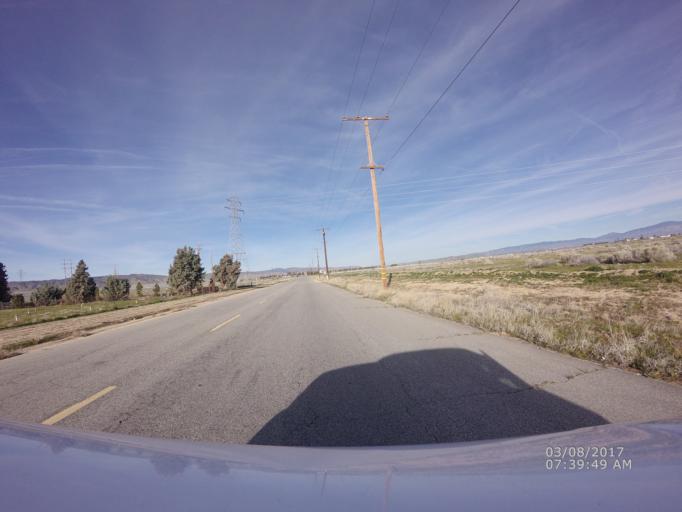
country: US
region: California
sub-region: Los Angeles County
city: Leona Valley
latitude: 34.7038
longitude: -118.2974
